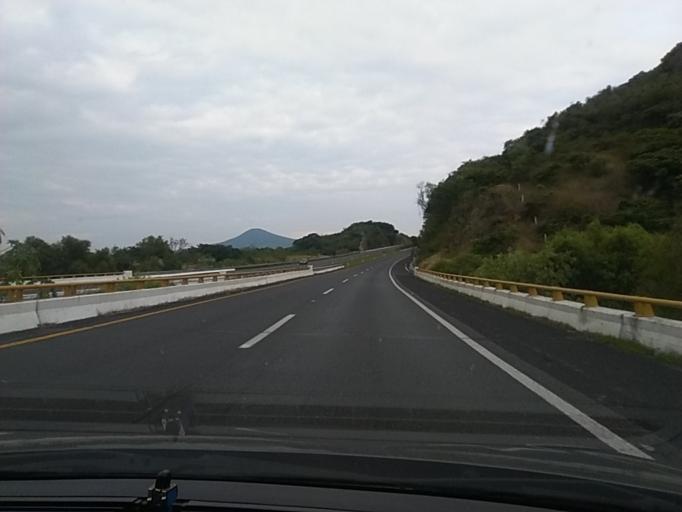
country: MX
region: Michoacan
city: Panindicuaro de la Reforma
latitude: 19.9745
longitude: -101.7462
